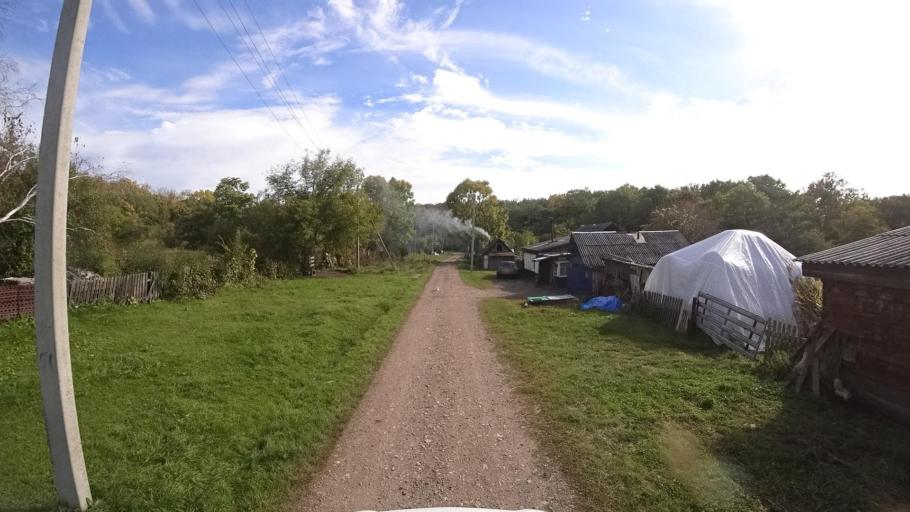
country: RU
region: Primorskiy
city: Dostoyevka
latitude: 44.2926
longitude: 133.4486
